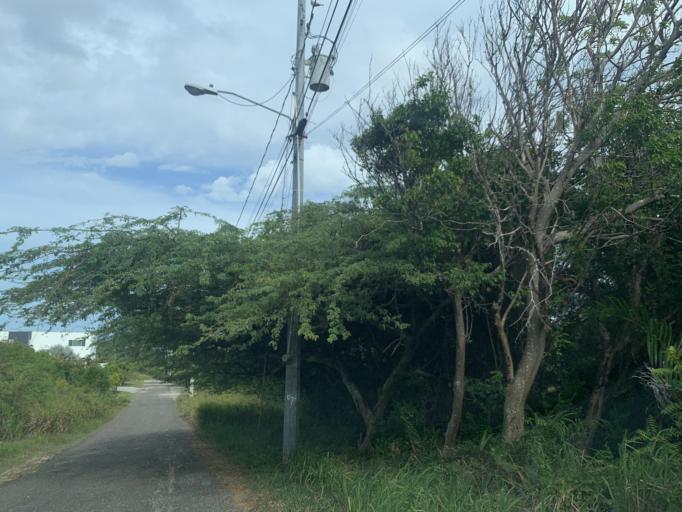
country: DO
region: Puerto Plata
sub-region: Puerto Plata
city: Puerto Plata
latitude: 19.8063
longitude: -70.7071
